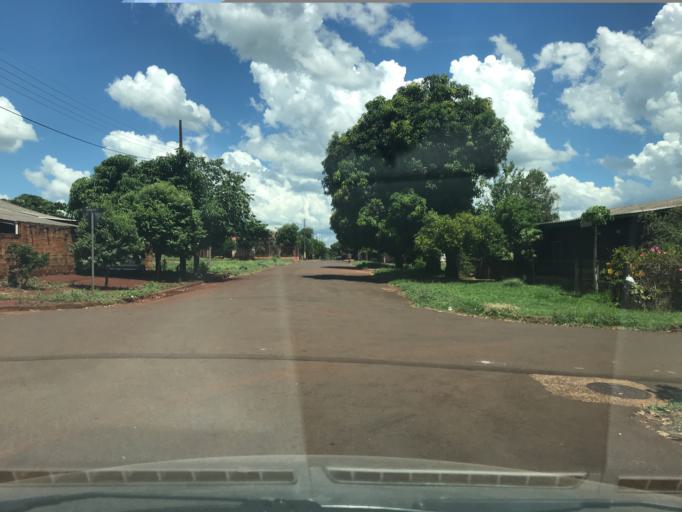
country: BR
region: Parana
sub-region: Palotina
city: Palotina
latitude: -24.2723
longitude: -53.8463
